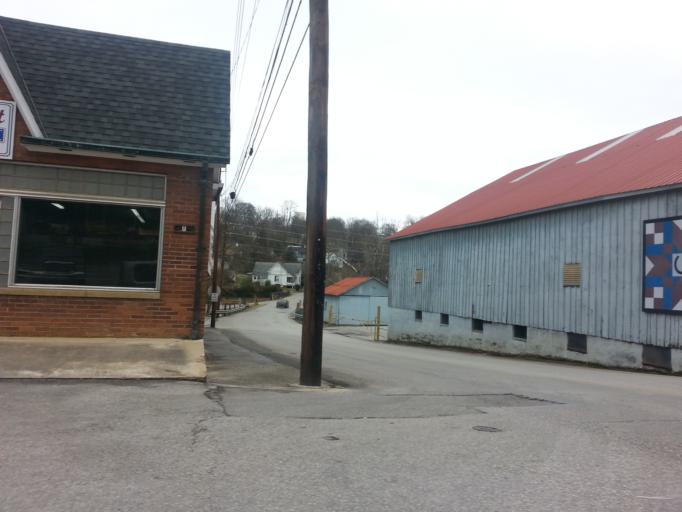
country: US
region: Tennessee
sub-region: Jefferson County
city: Jefferson City
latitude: 36.1269
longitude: -83.4925
